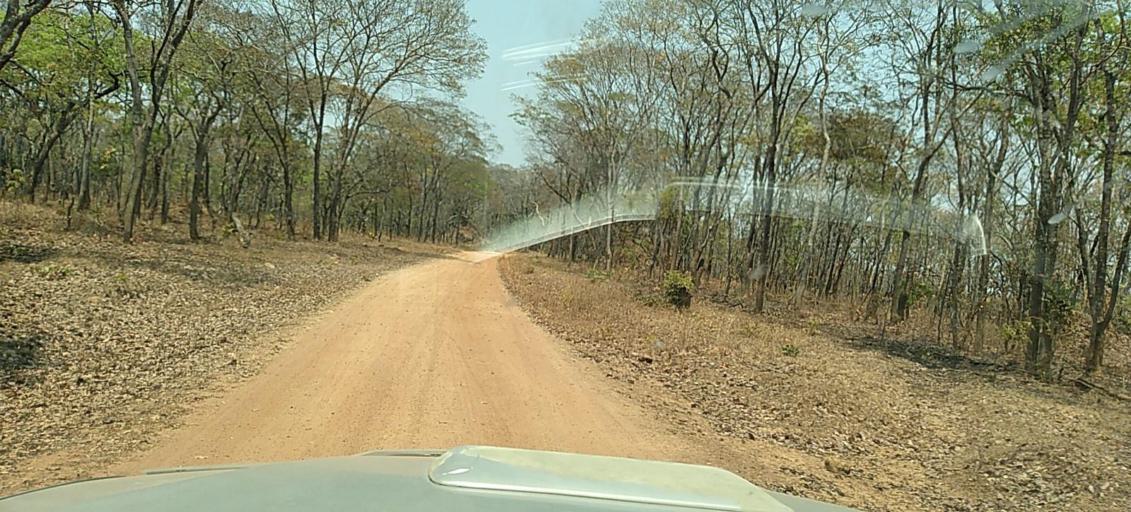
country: ZM
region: North-Western
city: Kasempa
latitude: -13.6096
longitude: 26.1946
